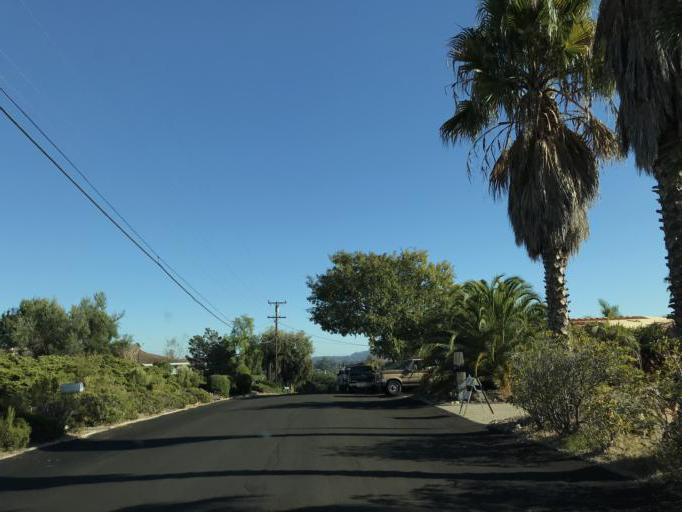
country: US
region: California
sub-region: Santa Barbara County
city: Goleta
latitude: 34.4623
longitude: -119.8207
